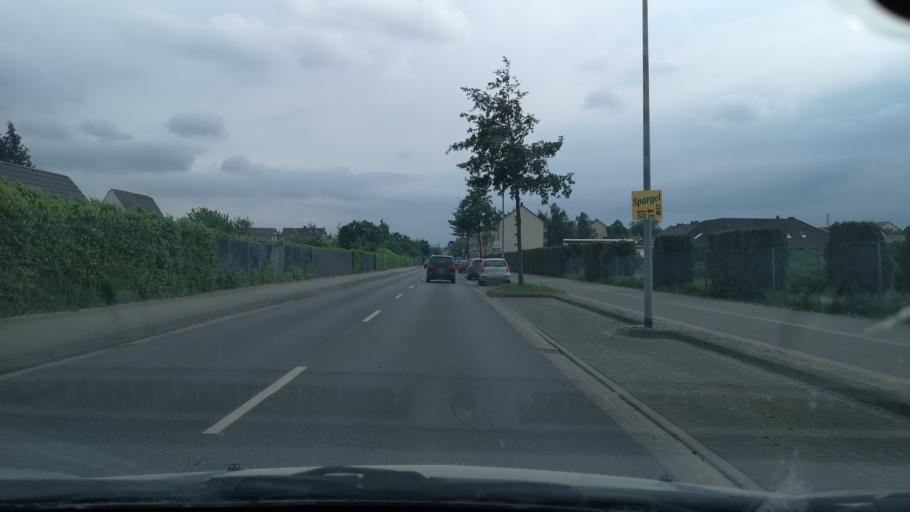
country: DE
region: Lower Saxony
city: Hannover
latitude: 52.4104
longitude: 9.6961
